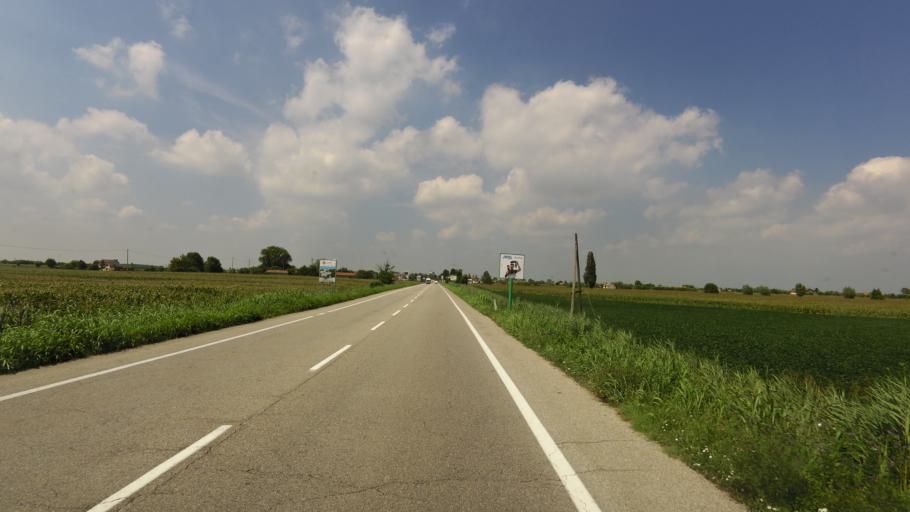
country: IT
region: Veneto
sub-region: Provincia di Padova
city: Codevigo
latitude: 45.2633
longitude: 12.1209
